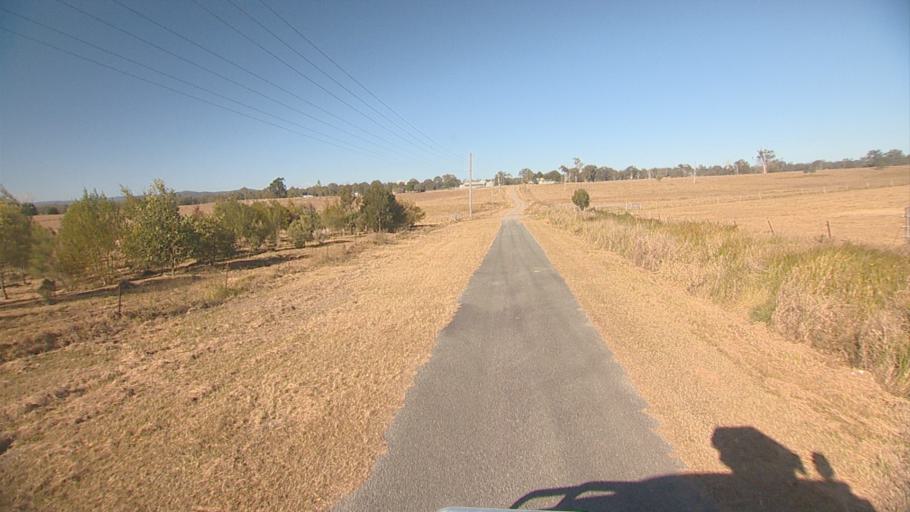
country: AU
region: Queensland
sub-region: Logan
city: North Maclean
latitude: -27.7661
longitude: 153.0472
